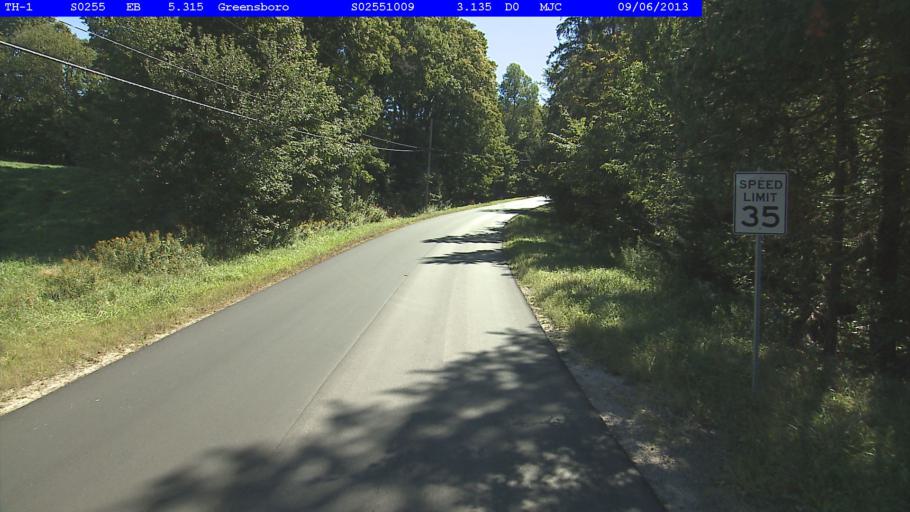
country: US
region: Vermont
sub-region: Caledonia County
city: Hardwick
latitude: 44.6022
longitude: -72.3074
